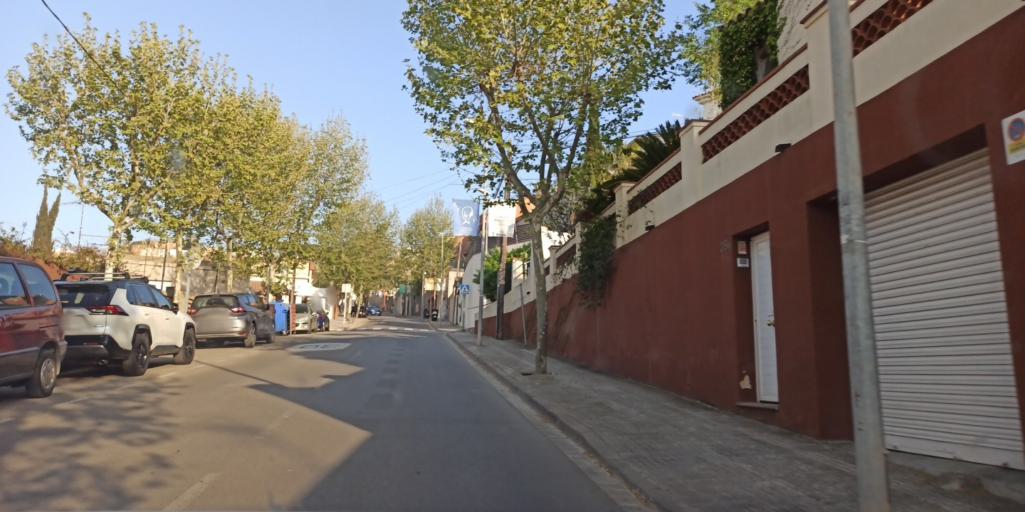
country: ES
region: Catalonia
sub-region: Provincia de Barcelona
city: Sant Just Desvern
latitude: 41.3873
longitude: 2.0782
